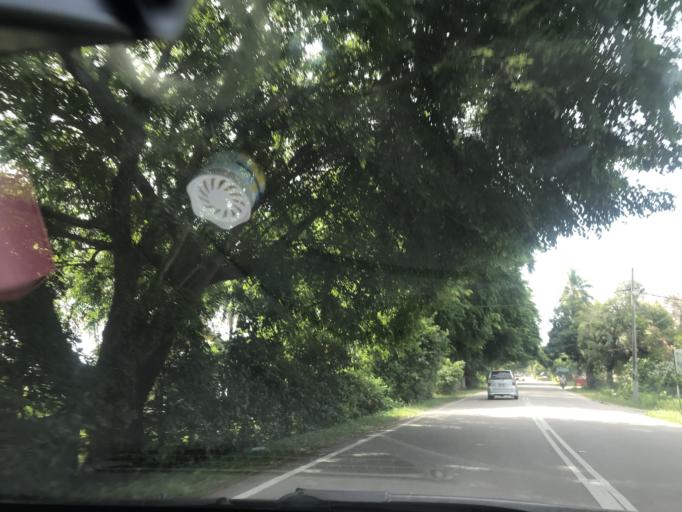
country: MY
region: Kelantan
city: Tumpat
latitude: 6.2141
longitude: 102.1285
